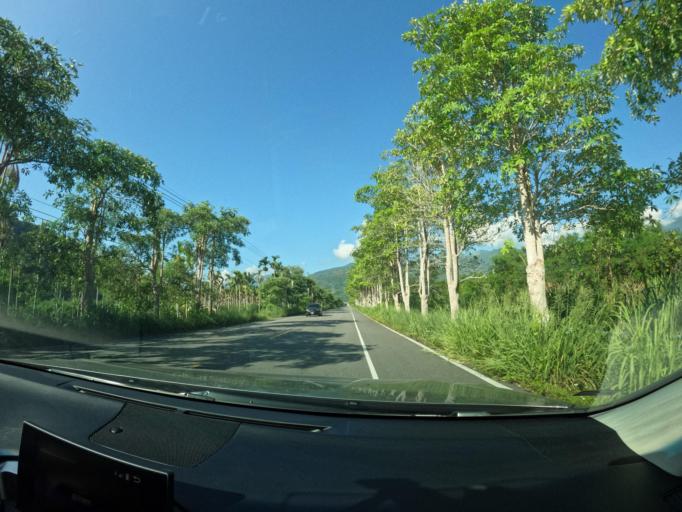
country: TW
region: Taiwan
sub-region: Hualien
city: Hualian
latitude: 23.4825
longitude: 121.3680
